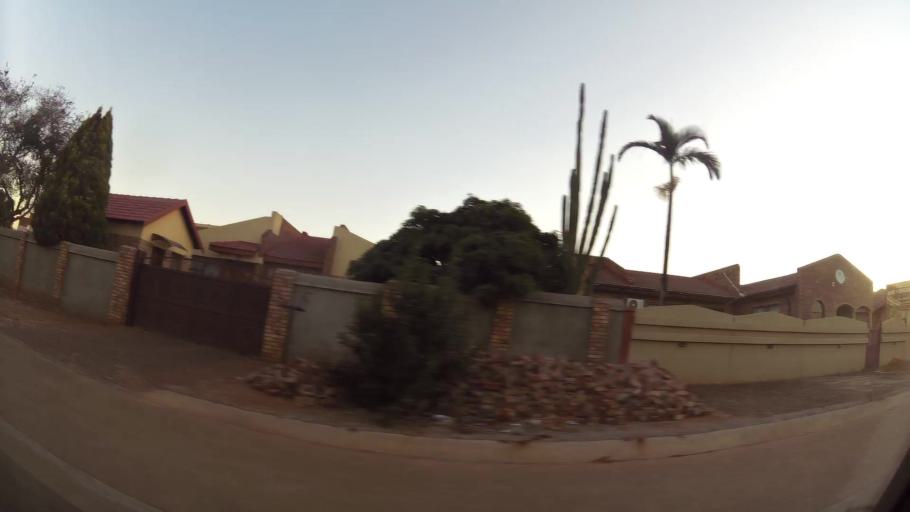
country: ZA
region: North-West
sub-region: Bojanala Platinum District Municipality
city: Rustenburg
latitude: -25.6547
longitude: 27.2099
